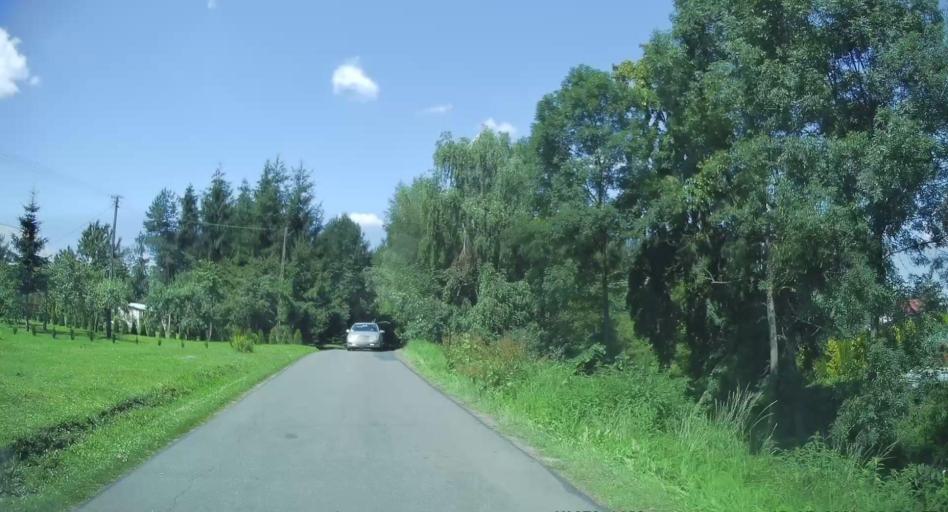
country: PL
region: Subcarpathian Voivodeship
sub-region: Powiat jaroslawski
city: Sosnica
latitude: 49.8643
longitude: 22.8729
